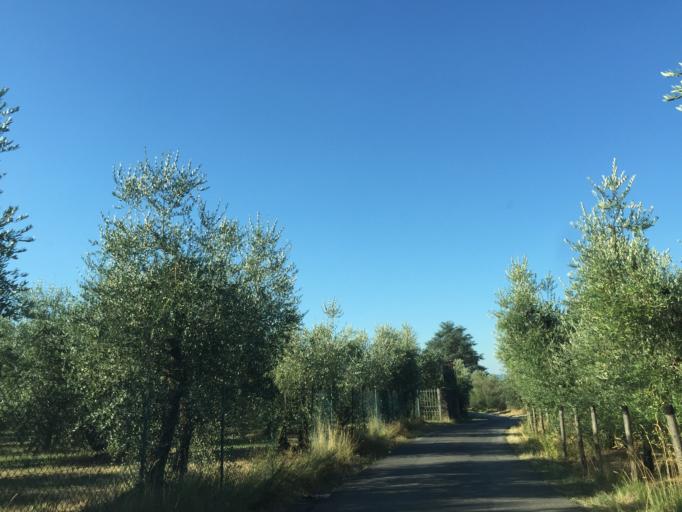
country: IT
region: Tuscany
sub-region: Provincia di Pistoia
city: Pistoia
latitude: 43.9465
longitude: 10.9444
